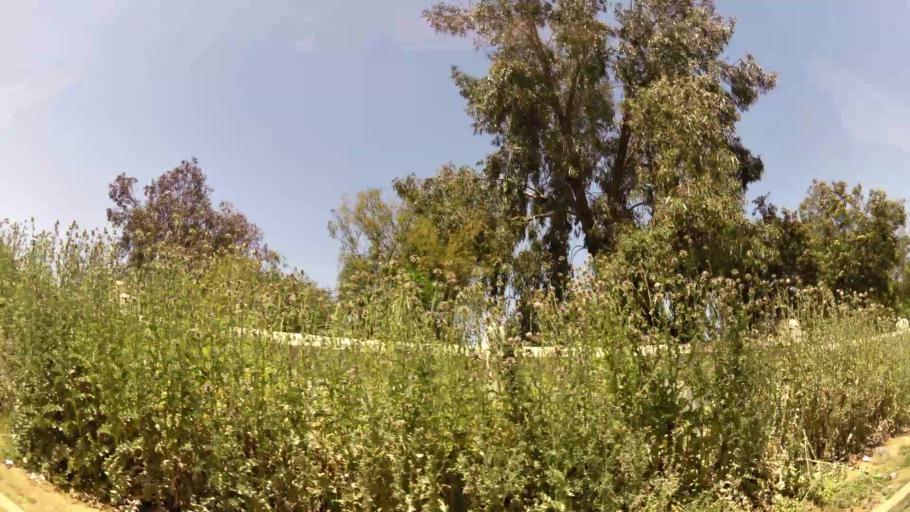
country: MA
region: Rabat-Sale-Zemmour-Zaer
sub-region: Khemisset
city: Khemisset
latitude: 33.8327
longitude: -6.0900
